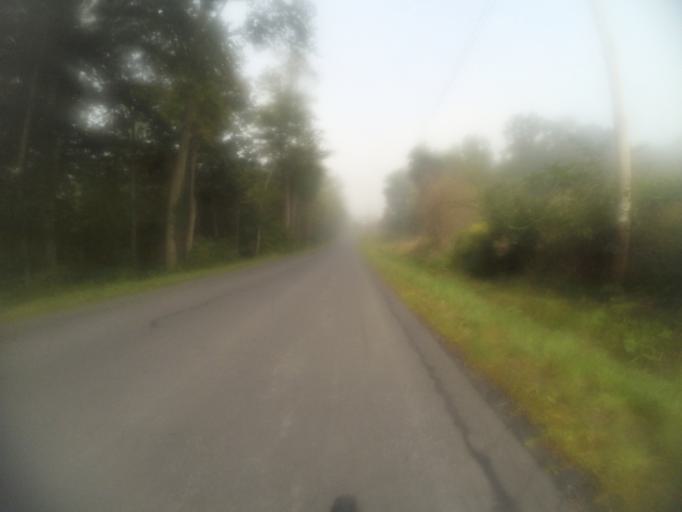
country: US
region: Pennsylvania
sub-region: Centre County
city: Zion
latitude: 40.8790
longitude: -77.5558
